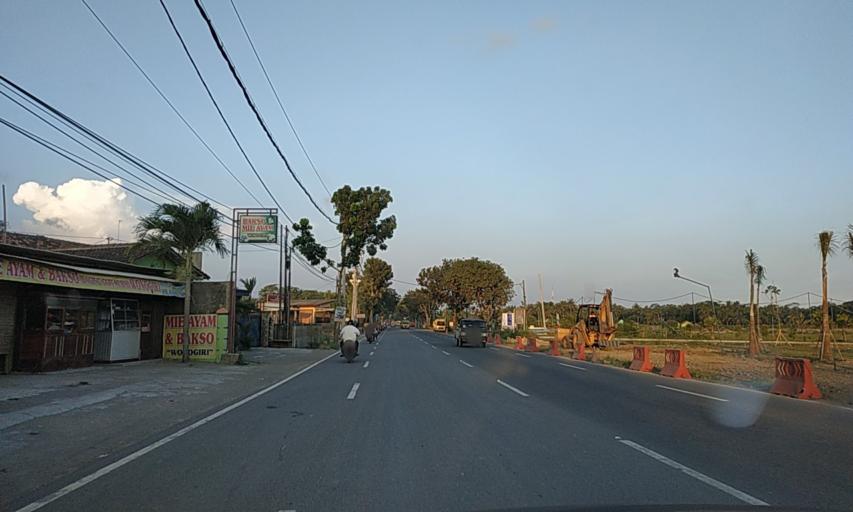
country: ID
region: Daerah Istimewa Yogyakarta
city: Srandakan
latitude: -7.8863
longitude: 110.0650
